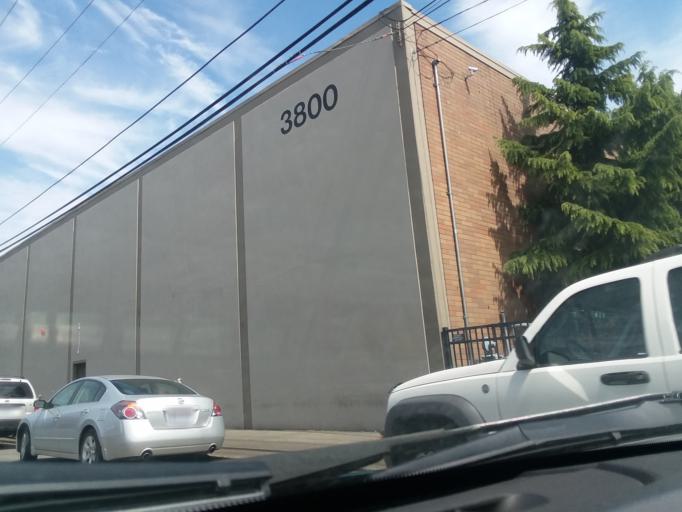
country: US
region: Washington
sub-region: King County
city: Seattle
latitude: 47.5695
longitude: -122.3341
